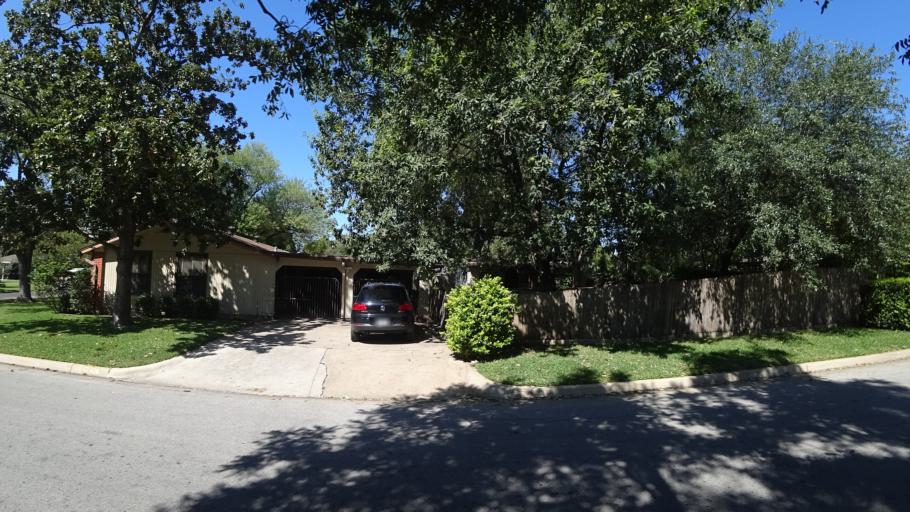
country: US
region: Texas
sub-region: Travis County
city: Austin
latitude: 30.3086
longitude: -97.6997
